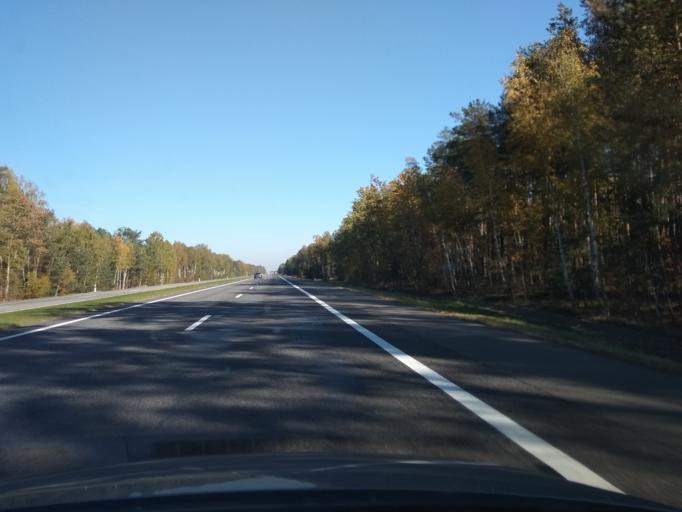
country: BY
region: Brest
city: Antopal'
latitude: 52.3720
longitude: 24.7454
